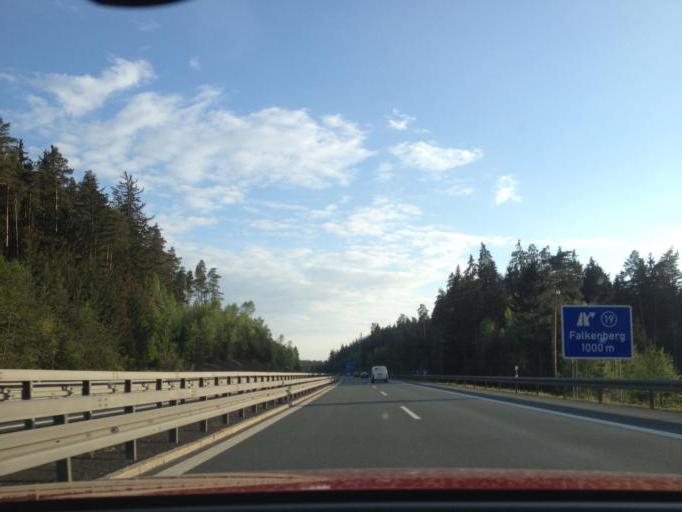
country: DE
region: Bavaria
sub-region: Upper Palatinate
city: Wiesau
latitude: 49.8712
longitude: 12.1887
